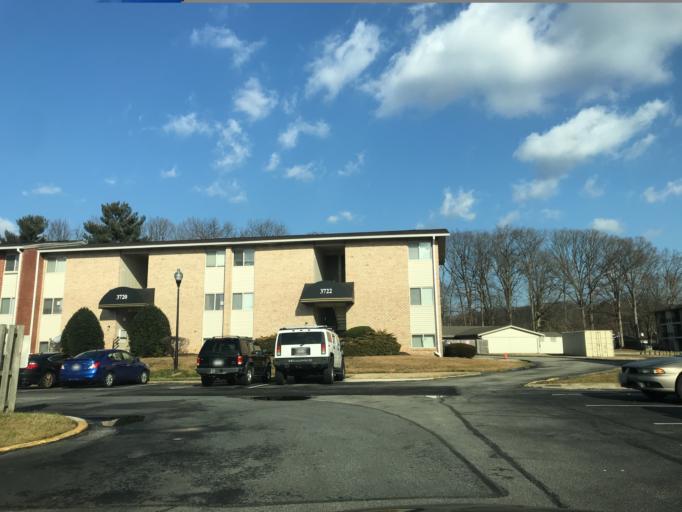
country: US
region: Maryland
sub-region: Baltimore County
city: Bowleys Quarters
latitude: 39.3311
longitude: -76.3927
